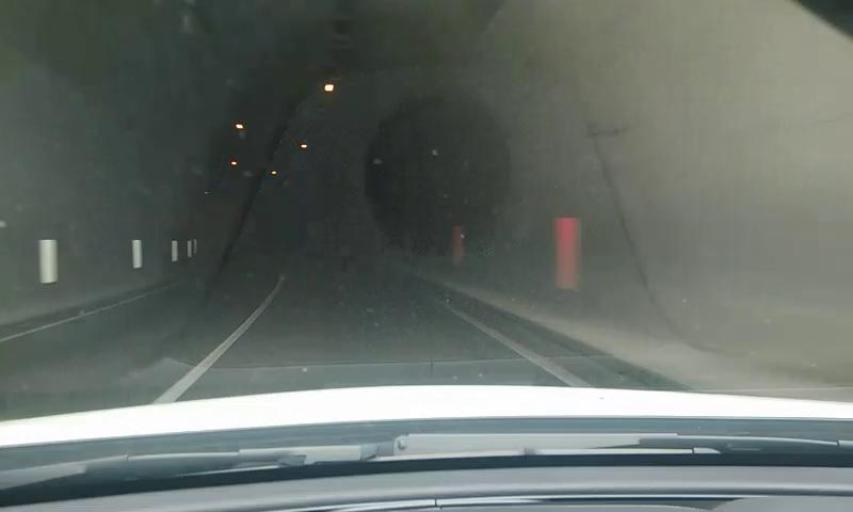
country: IT
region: Tuscany
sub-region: Provincia di Prato
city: Vaiano
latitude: 43.9136
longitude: 11.1245
